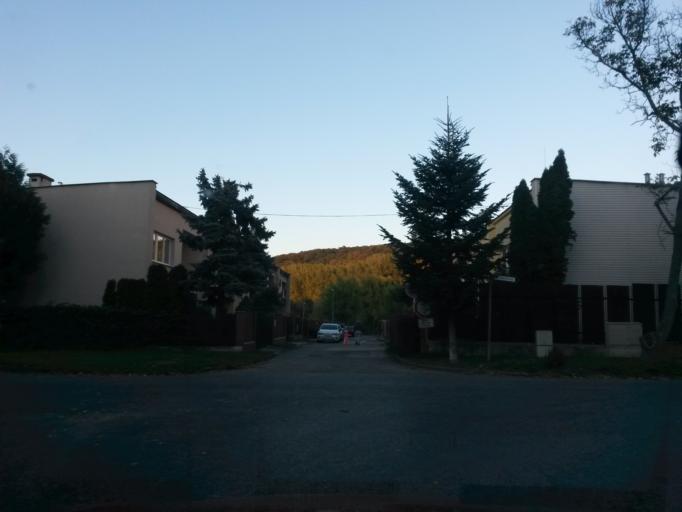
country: SK
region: Kosicky
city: Kosice
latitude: 48.6880
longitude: 21.2883
